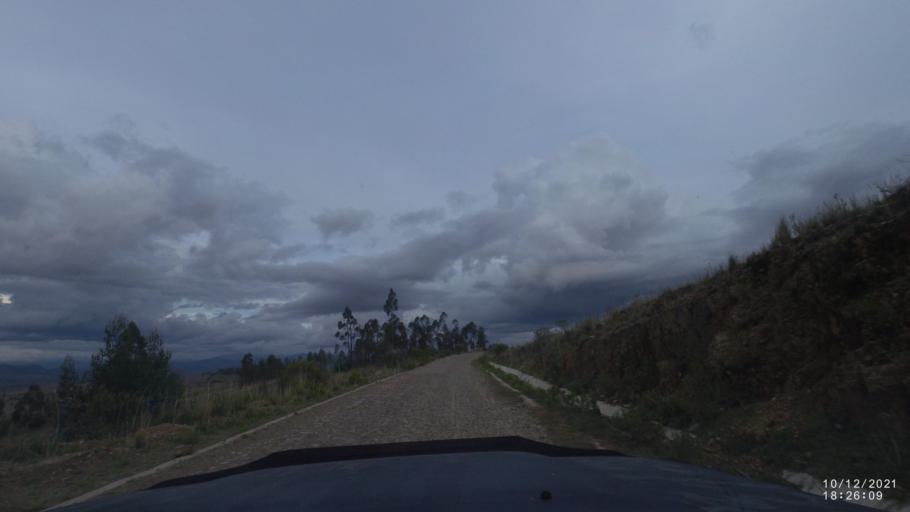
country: BO
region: Cochabamba
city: Tarata
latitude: -17.7960
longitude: -65.9737
